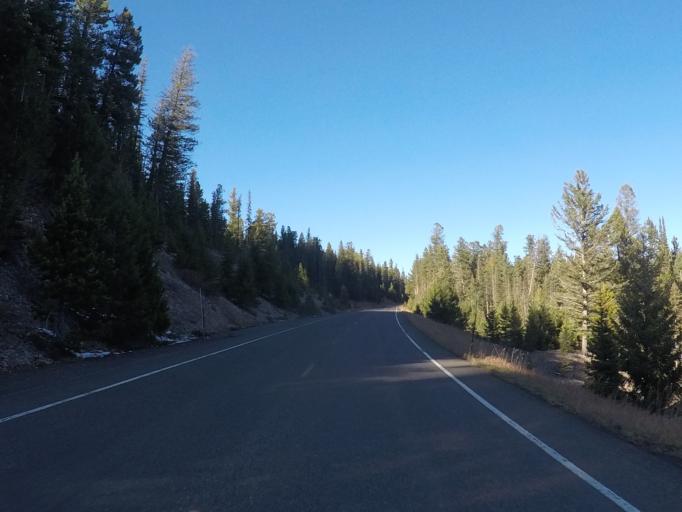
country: US
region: Montana
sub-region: Carbon County
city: Red Lodge
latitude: 44.9955
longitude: -109.8553
